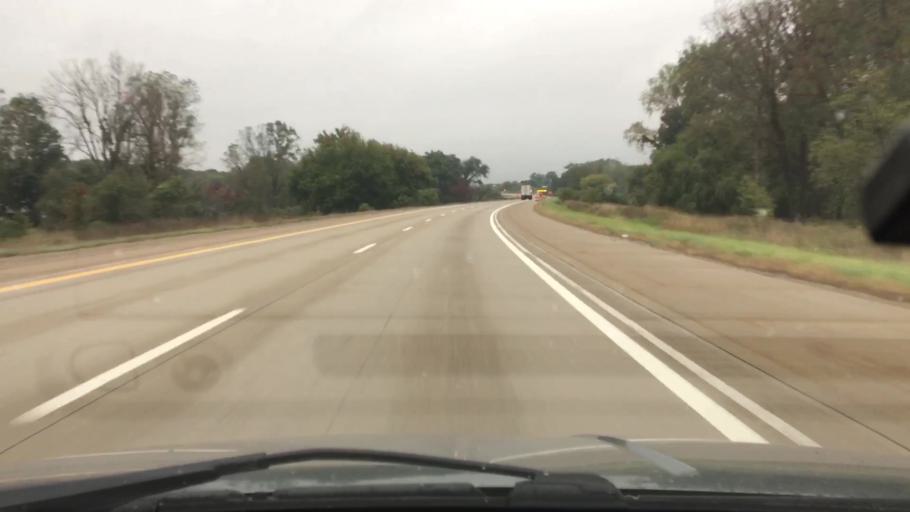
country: US
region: Michigan
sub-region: Jackson County
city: Michigan Center
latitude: 42.2818
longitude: -84.2930
